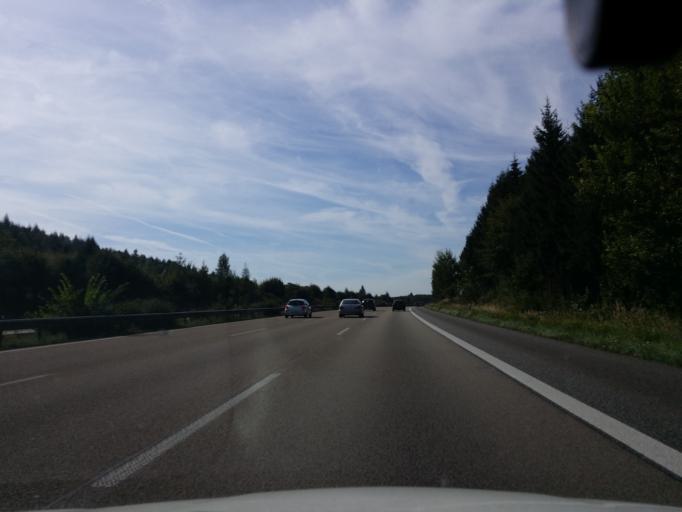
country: DE
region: Rheinland-Pfalz
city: Kleinmaischeid
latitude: 50.5242
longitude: 7.6215
